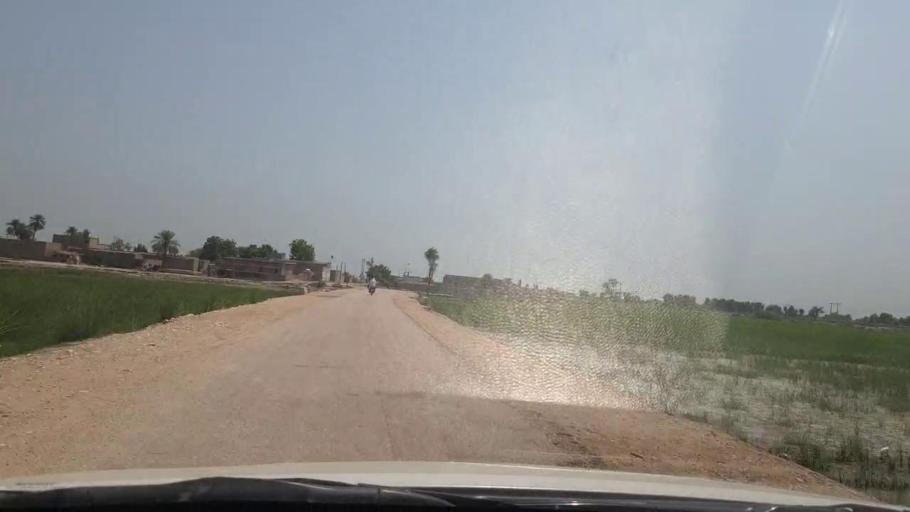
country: PK
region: Sindh
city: Rustam jo Goth
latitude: 28.0265
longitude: 68.7994
